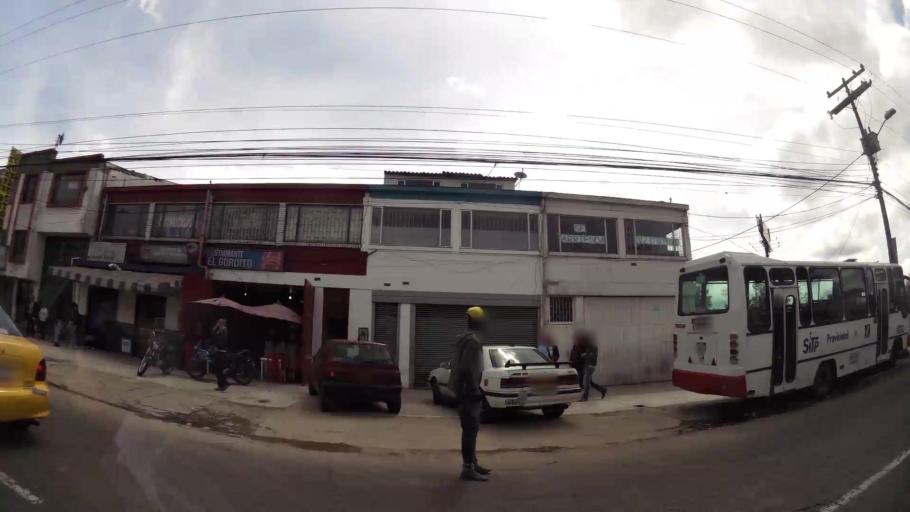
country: CO
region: Bogota D.C.
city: Bogota
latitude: 4.6864
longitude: -74.1138
